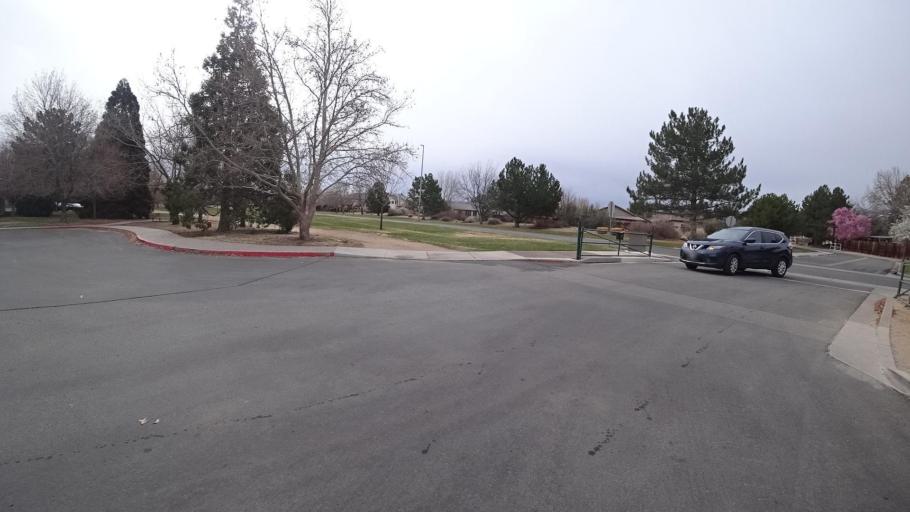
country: US
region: Nevada
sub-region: Washoe County
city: Reno
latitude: 39.5458
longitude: -119.8262
